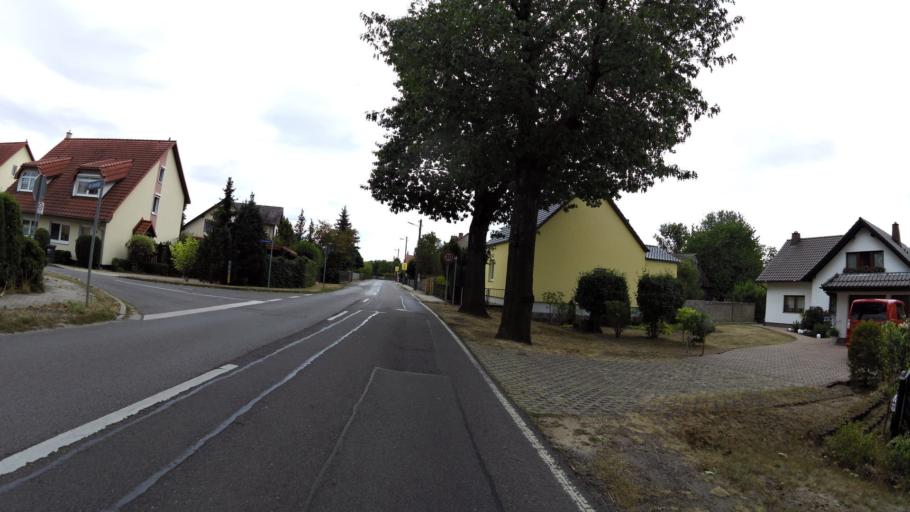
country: DE
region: Brandenburg
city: Cottbus
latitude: 51.7239
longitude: 14.4163
